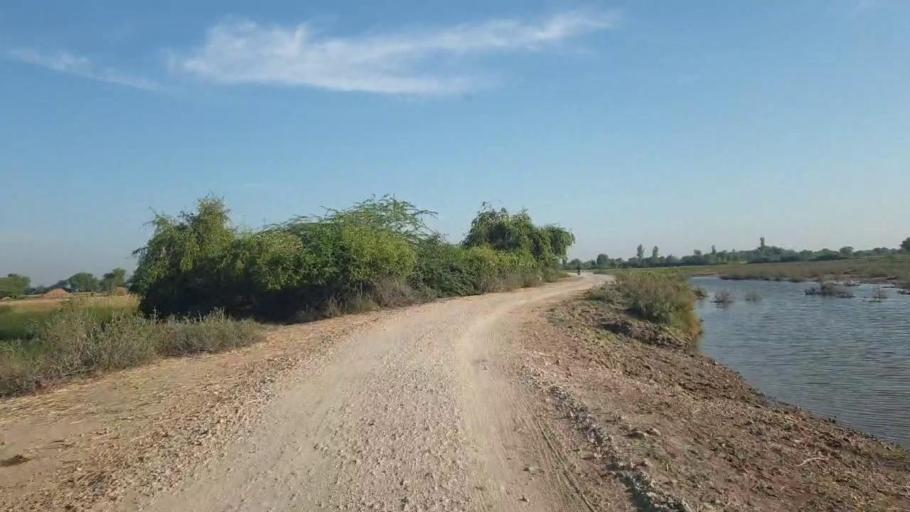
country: PK
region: Sindh
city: Talhar
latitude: 24.8215
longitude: 68.8388
